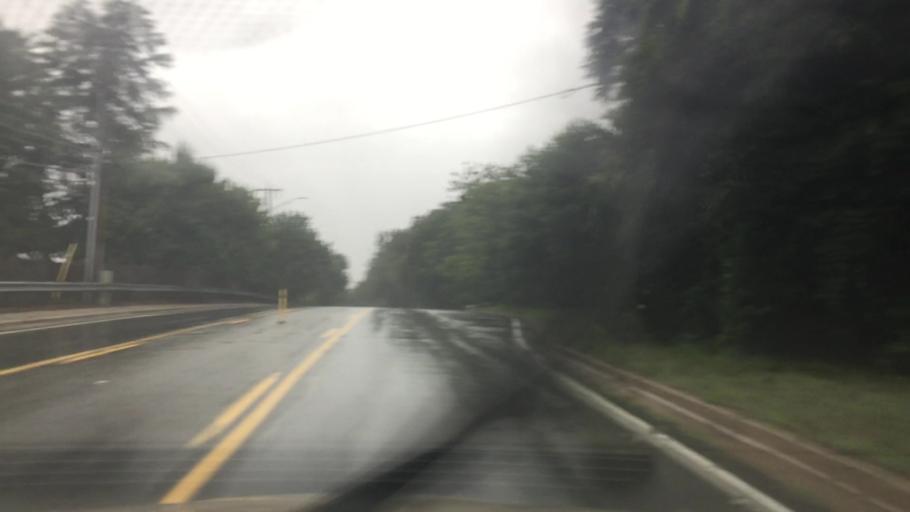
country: US
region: Maryland
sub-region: Anne Arundel County
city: Severn
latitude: 39.1360
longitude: -76.7157
